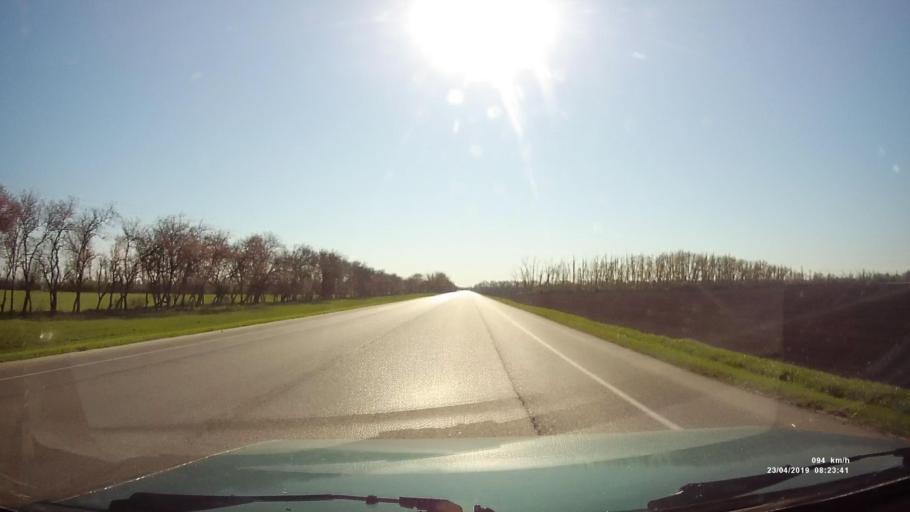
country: RU
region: Rostov
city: Tselina
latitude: 46.5317
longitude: 40.9334
